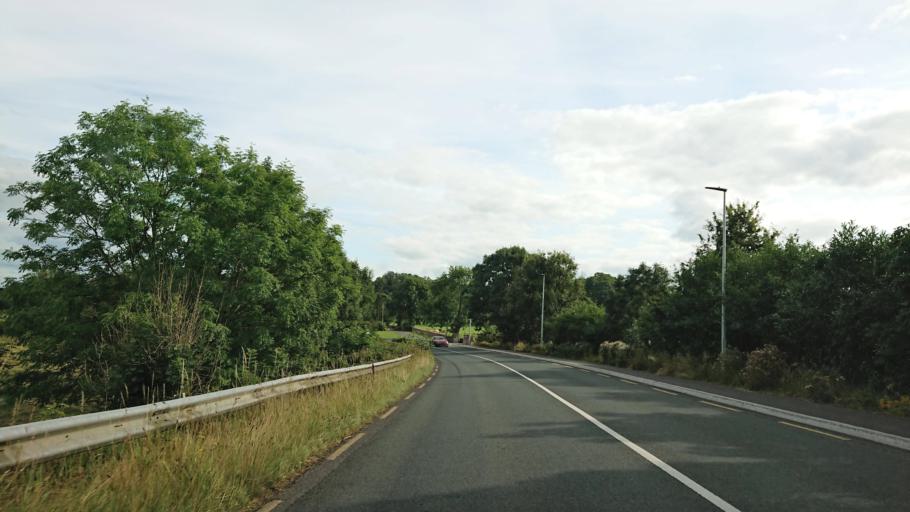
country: IE
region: Connaught
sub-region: County Leitrim
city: Carrick-on-Shannon
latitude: 53.9823
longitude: -8.0652
